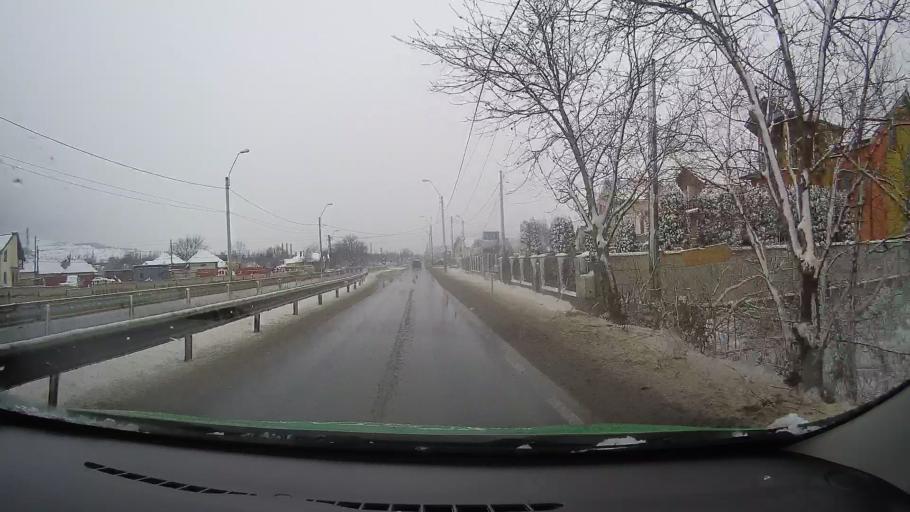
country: RO
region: Hunedoara
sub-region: Municipiul Hunedoara
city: Pestisu Mare
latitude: 45.7997
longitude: 22.9214
